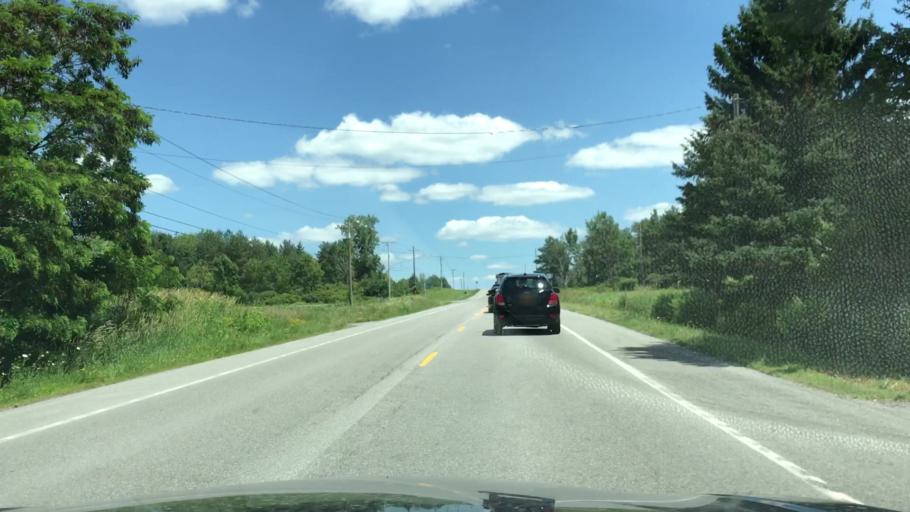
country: US
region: New York
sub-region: Wyoming County
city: Attica
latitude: 42.7706
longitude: -78.3542
